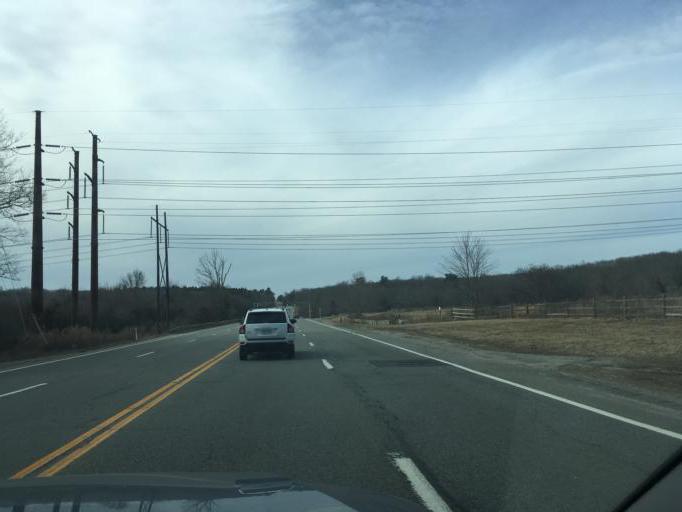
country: US
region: Rhode Island
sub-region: Providence County
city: Smithfield
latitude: 41.9206
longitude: -71.5248
